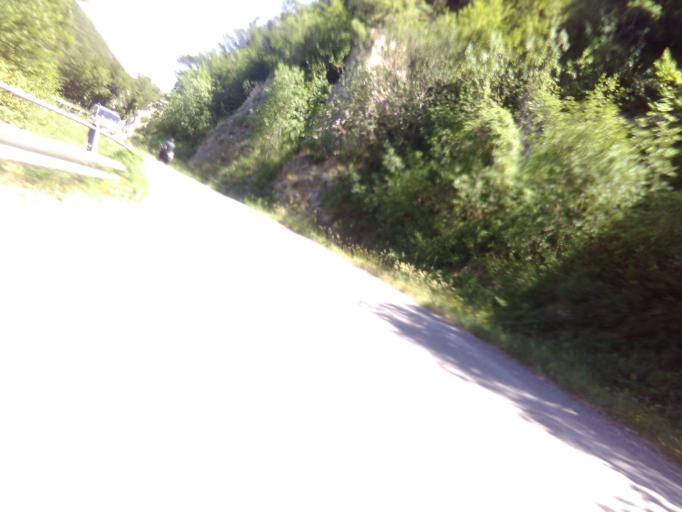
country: IT
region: Emilia-Romagna
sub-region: Provincia di Parma
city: Calestano
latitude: 44.5866
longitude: 10.1040
